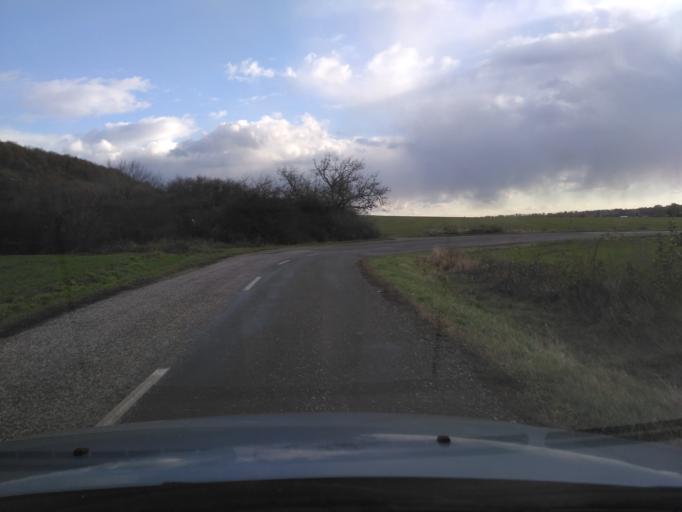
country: HU
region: Borsod-Abauj-Zemplen
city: Satoraljaujhely
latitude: 48.4058
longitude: 21.7121
